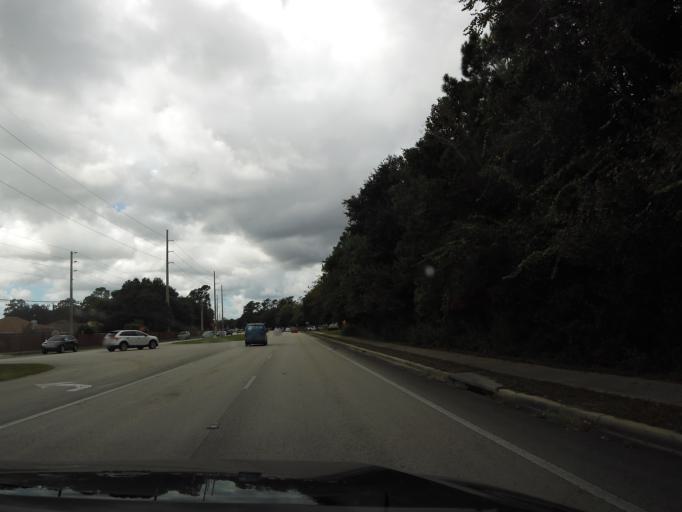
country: US
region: Florida
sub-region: Clay County
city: Lakeside
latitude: 30.1019
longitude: -81.7386
